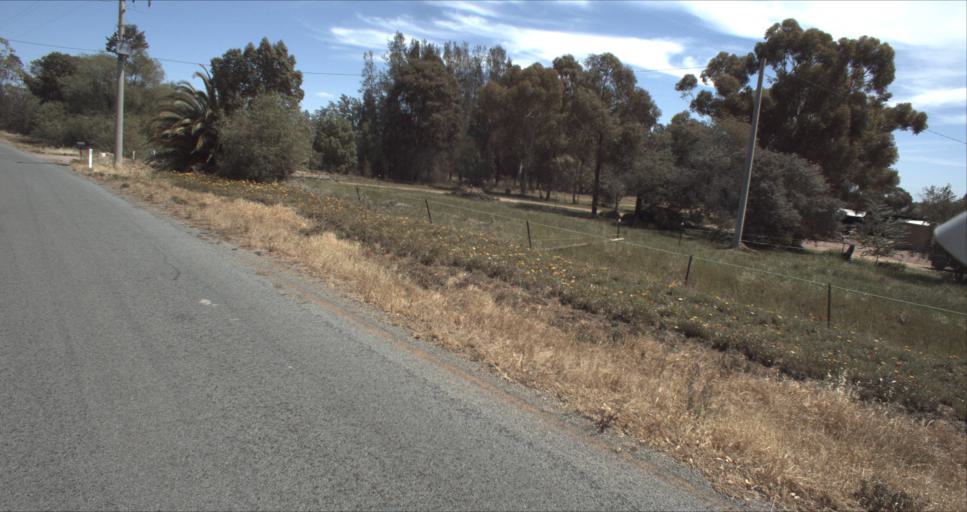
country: AU
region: New South Wales
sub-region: Leeton
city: Leeton
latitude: -34.5721
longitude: 146.4337
